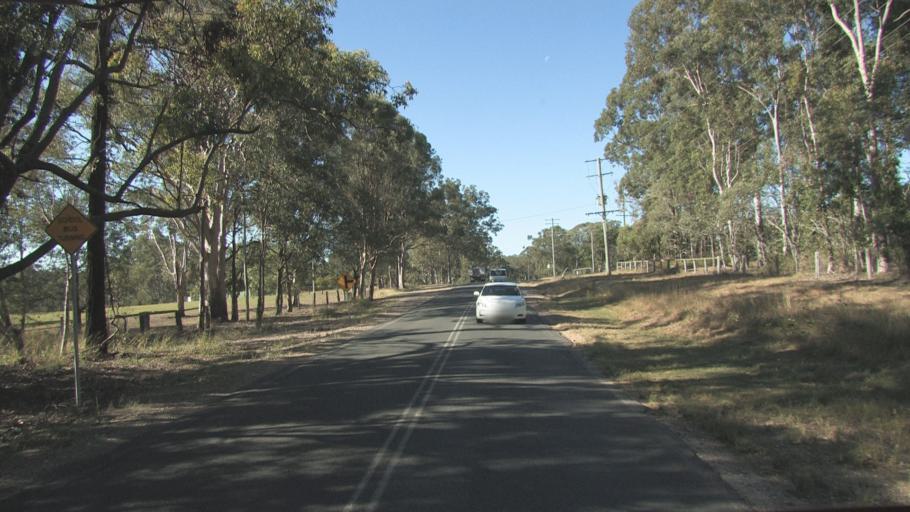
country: AU
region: Queensland
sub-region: Logan
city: Waterford West
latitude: -27.7400
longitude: 153.1464
